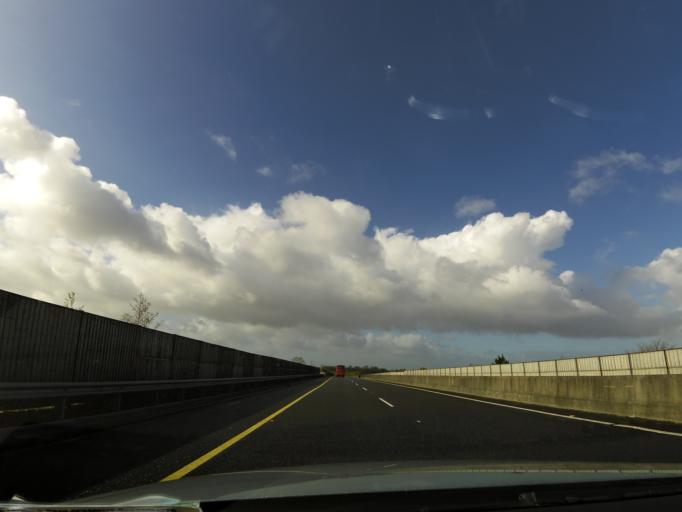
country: IE
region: Munster
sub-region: County Limerick
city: Castleconnell
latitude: 52.7055
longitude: -8.4833
